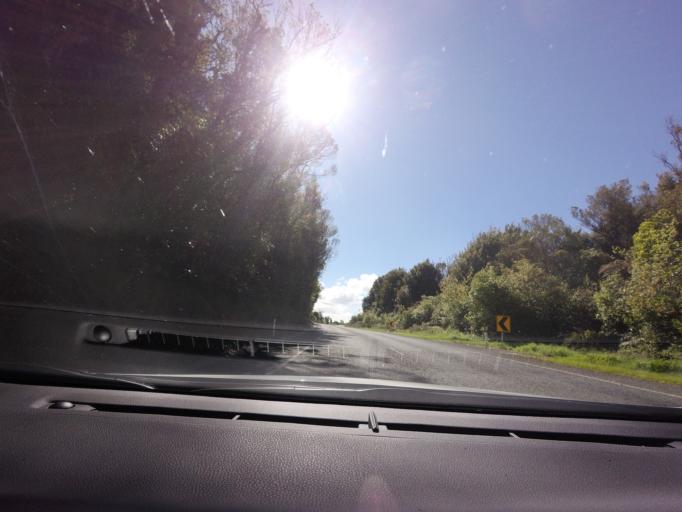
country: NZ
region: Bay of Plenty
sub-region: Rotorua District
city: Rotorua
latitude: -38.0575
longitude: 176.0898
